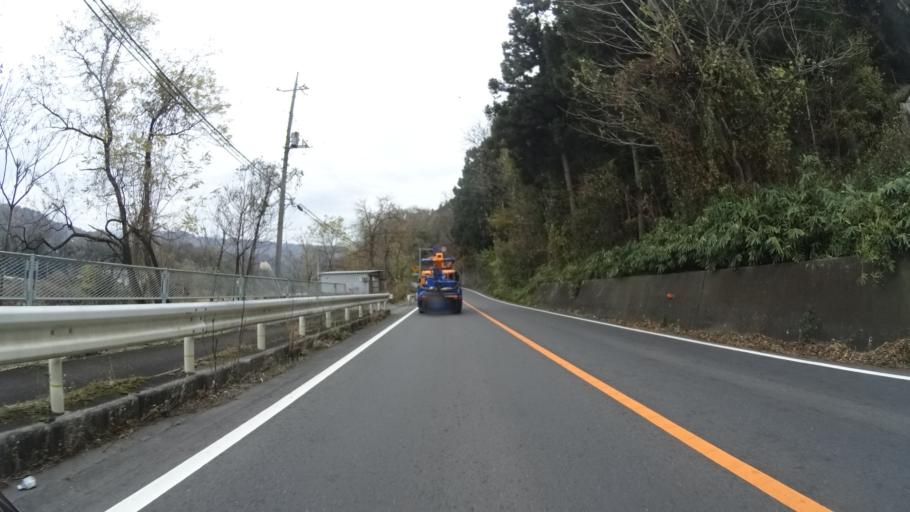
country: JP
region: Gunma
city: Numata
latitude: 36.6096
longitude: 139.0421
